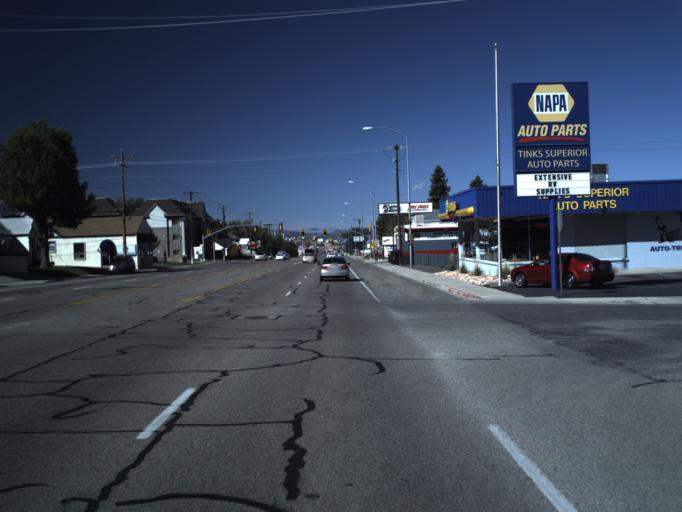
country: US
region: Utah
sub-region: Iron County
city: Cedar City
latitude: 37.6810
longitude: -113.0650
